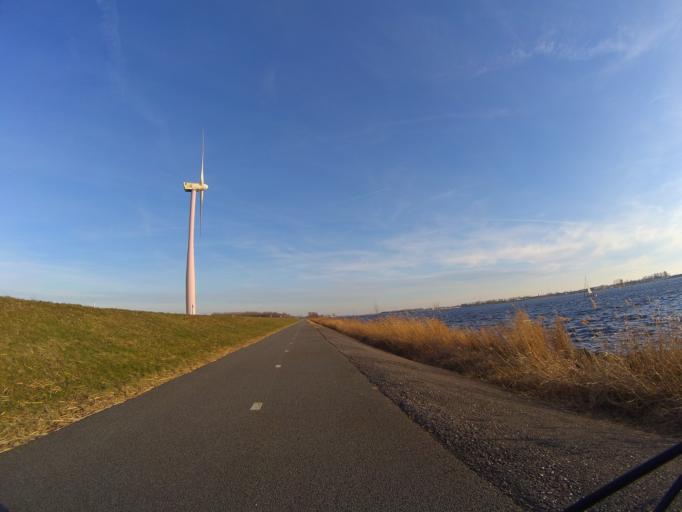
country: NL
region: Utrecht
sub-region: Gemeente Bunschoten
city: Spakenburg
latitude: 52.2704
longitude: 5.3747
